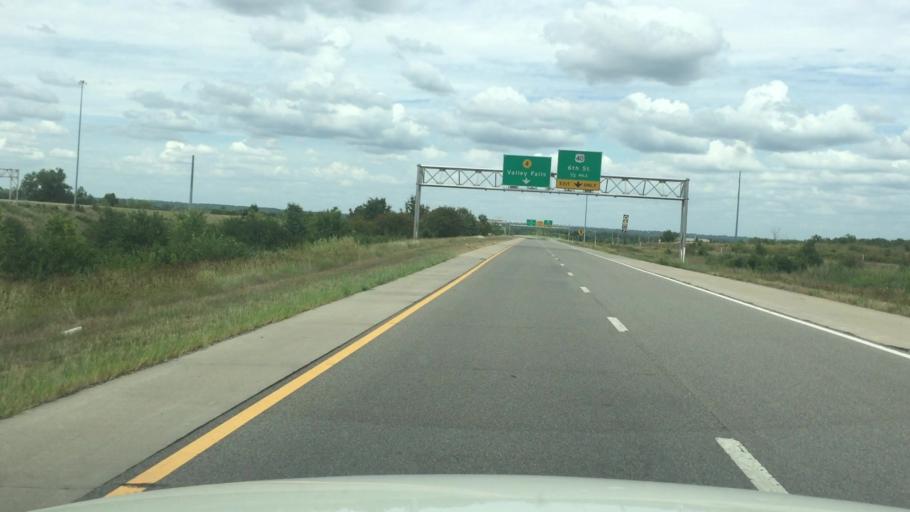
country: US
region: Kansas
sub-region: Shawnee County
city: Topeka
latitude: 39.0379
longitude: -95.6051
